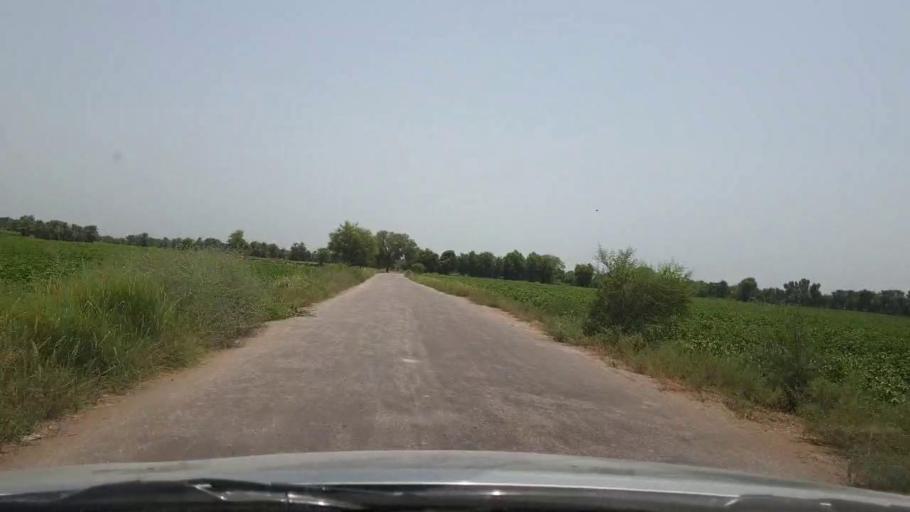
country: PK
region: Sindh
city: Pano Aqil
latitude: 27.8803
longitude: 69.1466
